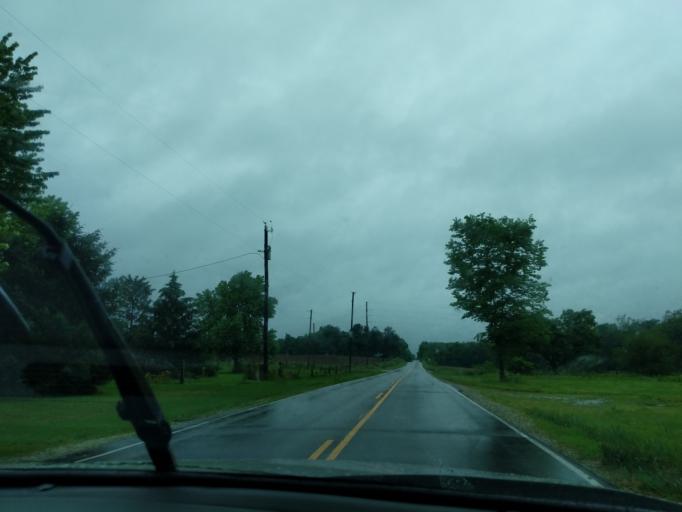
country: US
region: Indiana
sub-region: Madison County
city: Lapel
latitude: 40.0670
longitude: -85.8809
